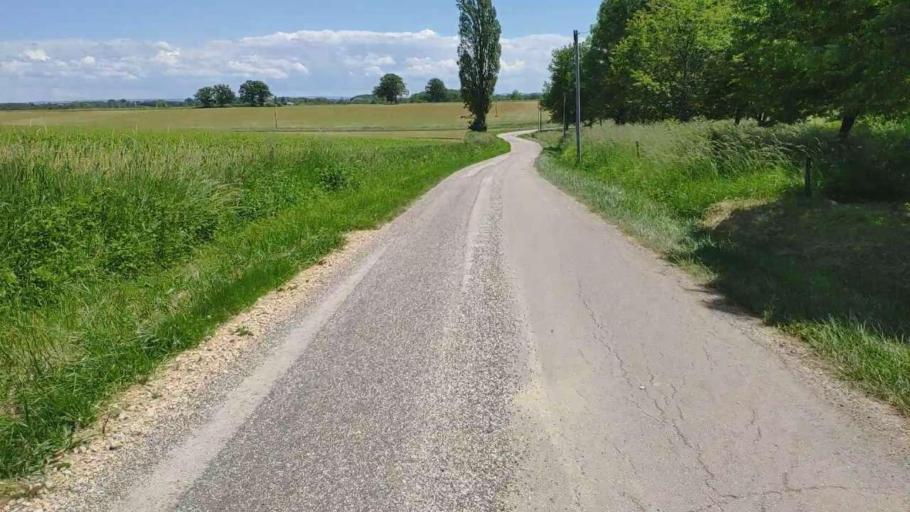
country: FR
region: Franche-Comte
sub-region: Departement du Jura
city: Bletterans
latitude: 46.7899
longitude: 5.3762
